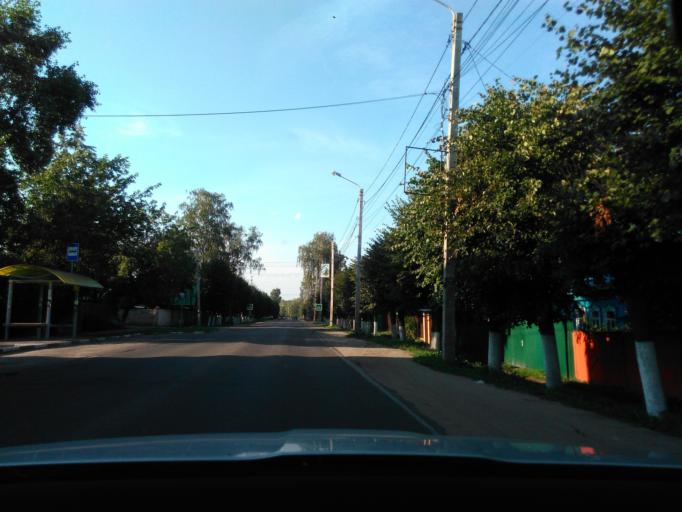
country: RU
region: Tverskaya
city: Konakovo
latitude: 56.7037
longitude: 36.7687
